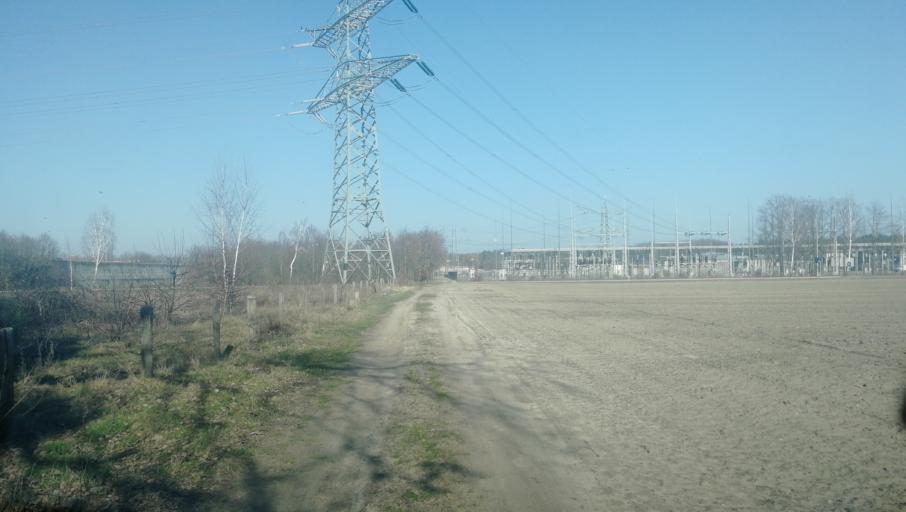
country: NL
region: Limburg
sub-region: Gemeente Venlo
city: Tegelen
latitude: 51.3881
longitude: 6.1115
